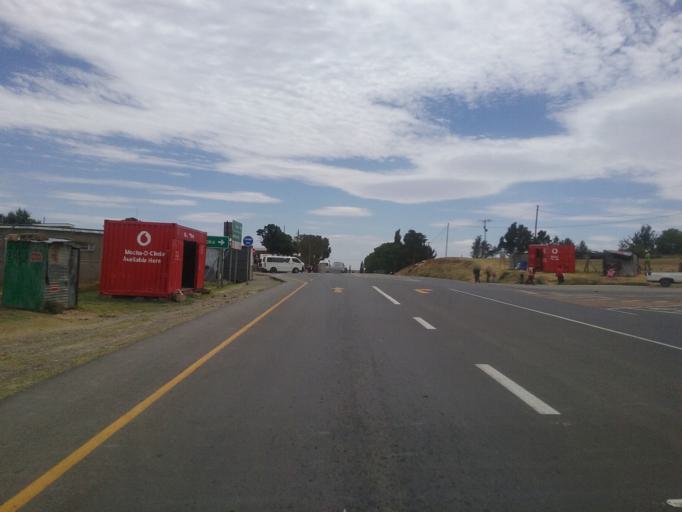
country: LS
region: Maseru
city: Maseru
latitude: -29.4887
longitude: 27.5271
